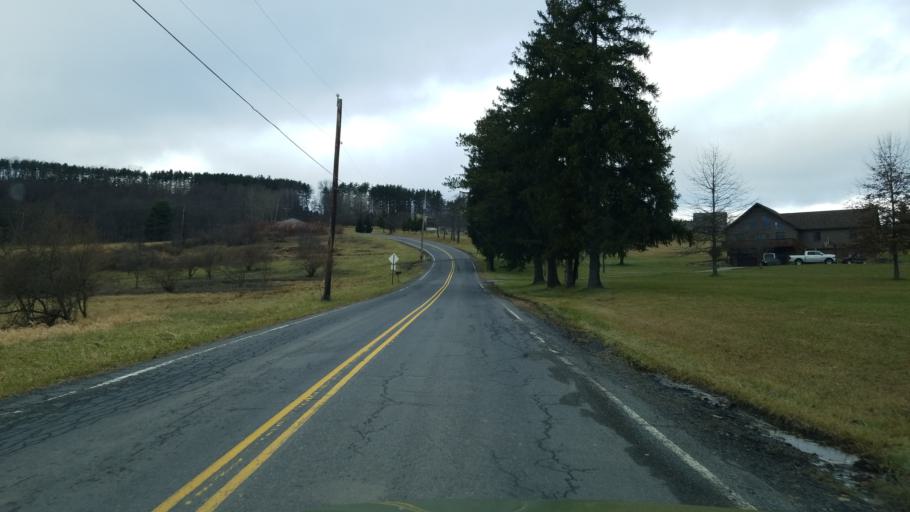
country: US
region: Pennsylvania
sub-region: Clearfield County
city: Hyde
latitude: 41.0358
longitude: -78.4893
